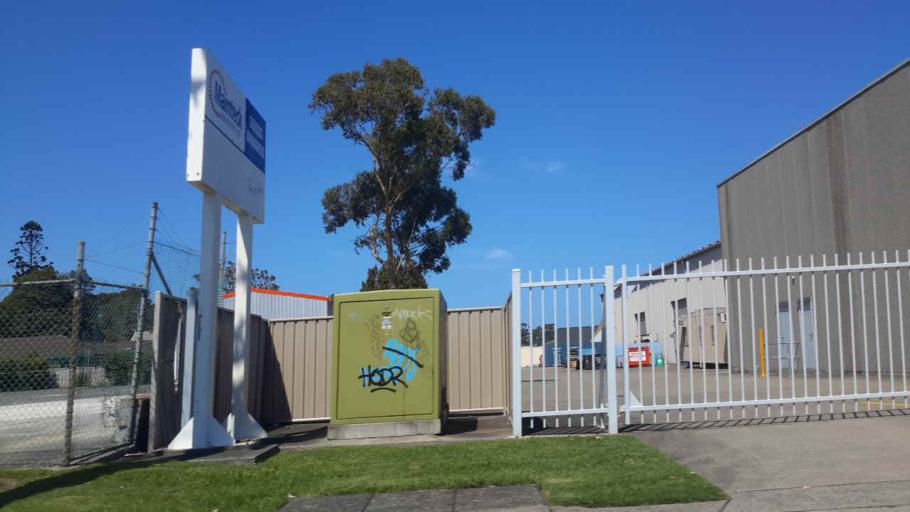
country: AU
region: New South Wales
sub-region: Wollongong
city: Fairy Meadow
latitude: -34.3863
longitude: 150.8944
